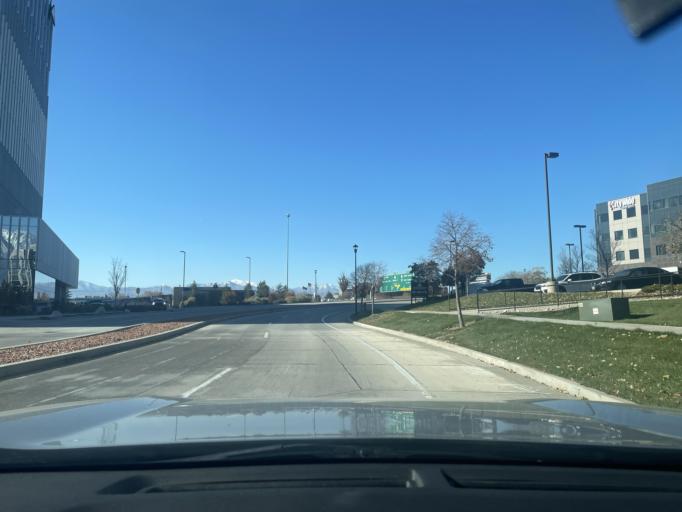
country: US
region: Utah
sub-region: Salt Lake County
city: Sandy City
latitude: 40.5731
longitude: -111.8981
